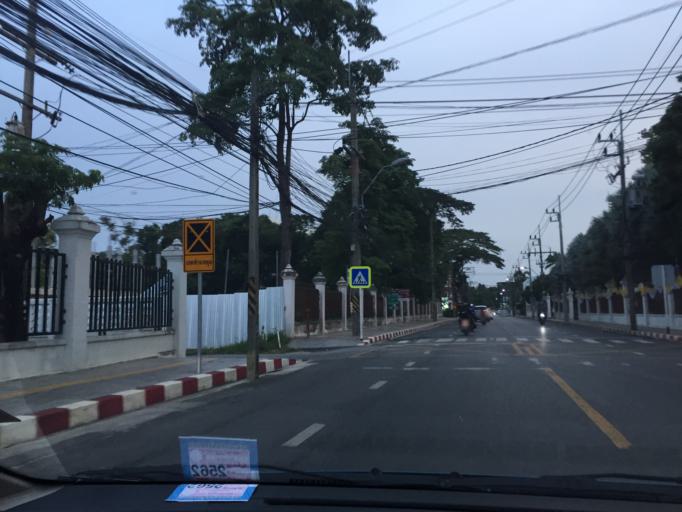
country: TH
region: Phuket
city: Wichit
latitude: 7.8928
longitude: 98.3859
